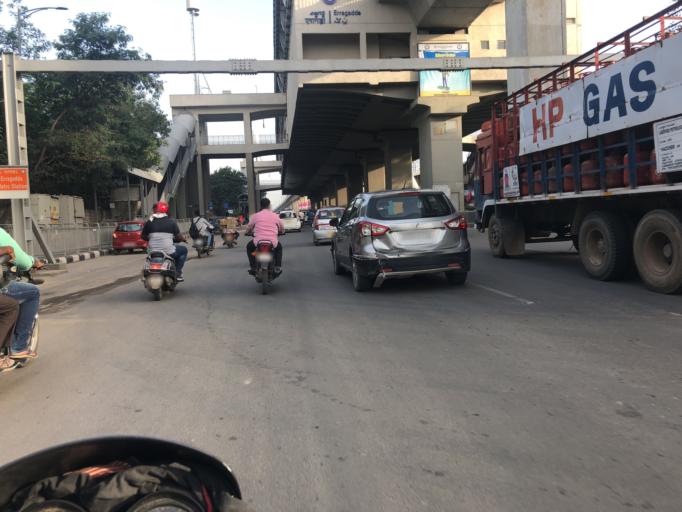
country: IN
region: Telangana
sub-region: Rangareddi
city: Kukatpalli
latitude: 17.4581
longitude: 78.4332
